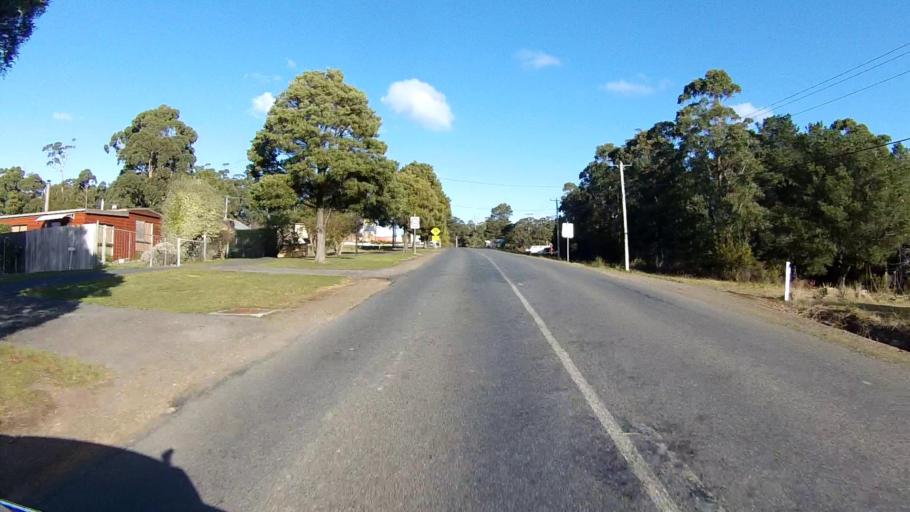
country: AU
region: Tasmania
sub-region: Clarence
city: Sandford
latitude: -43.1384
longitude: 147.8507
